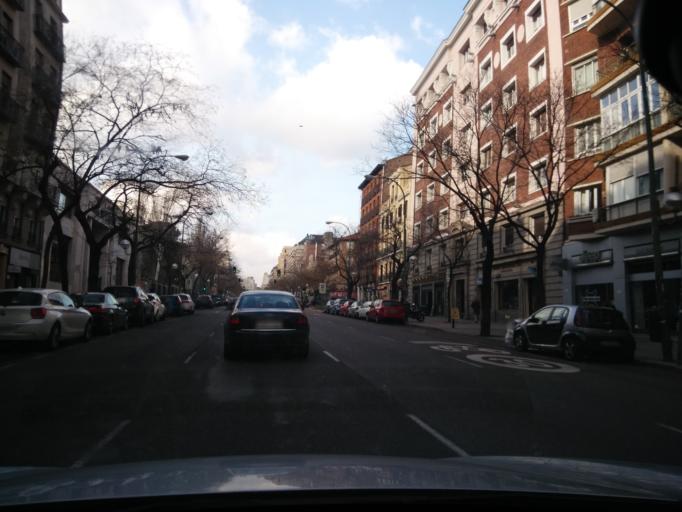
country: ES
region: Madrid
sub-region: Provincia de Madrid
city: Chamberi
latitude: 40.4387
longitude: -3.7003
